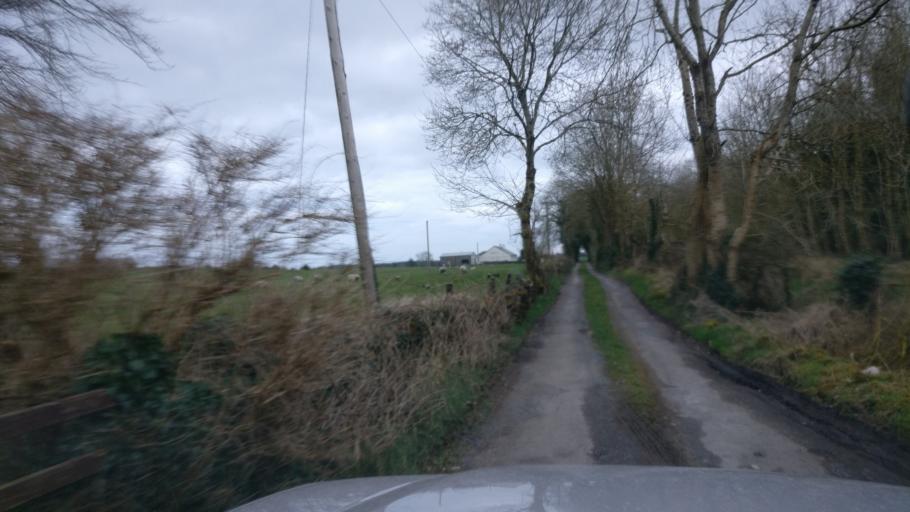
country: IE
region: Connaught
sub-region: County Galway
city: Loughrea
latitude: 53.2524
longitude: -8.4473
